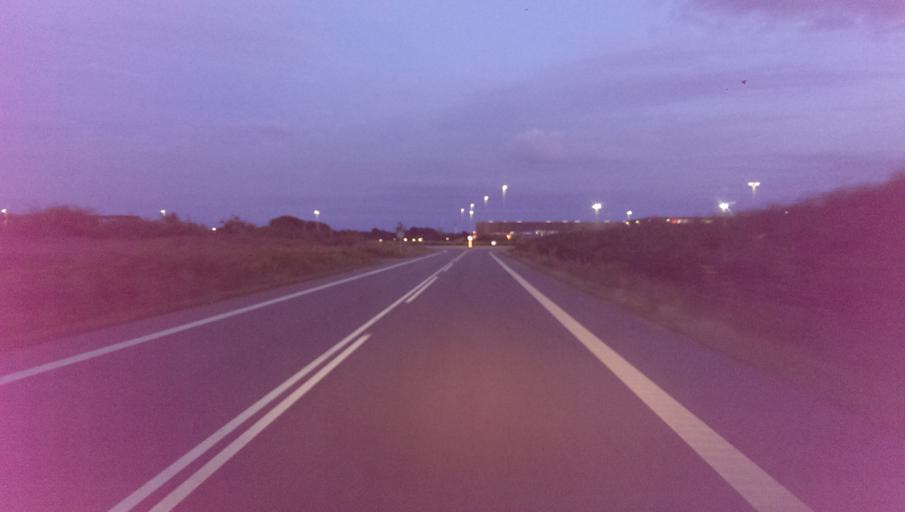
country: DK
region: South Denmark
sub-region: Esbjerg Kommune
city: Esbjerg
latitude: 55.5113
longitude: 8.4875
